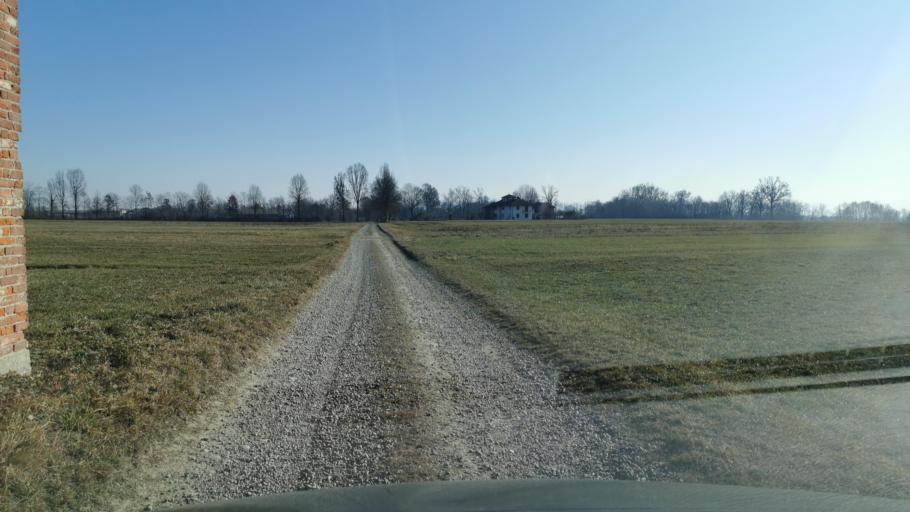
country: IT
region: Piedmont
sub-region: Provincia di Torino
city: Leini
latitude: 45.2151
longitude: 7.6964
